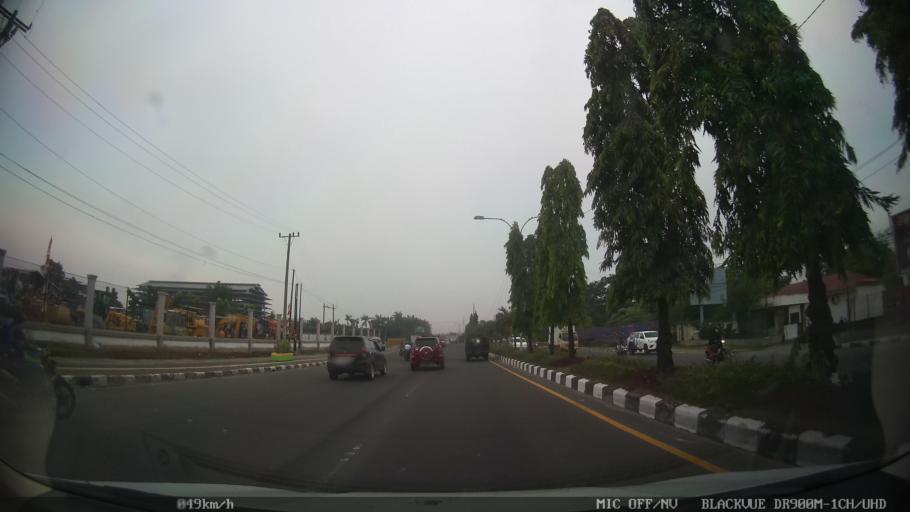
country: ID
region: North Sumatra
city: Deli Tua
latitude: 3.5370
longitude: 98.7129
